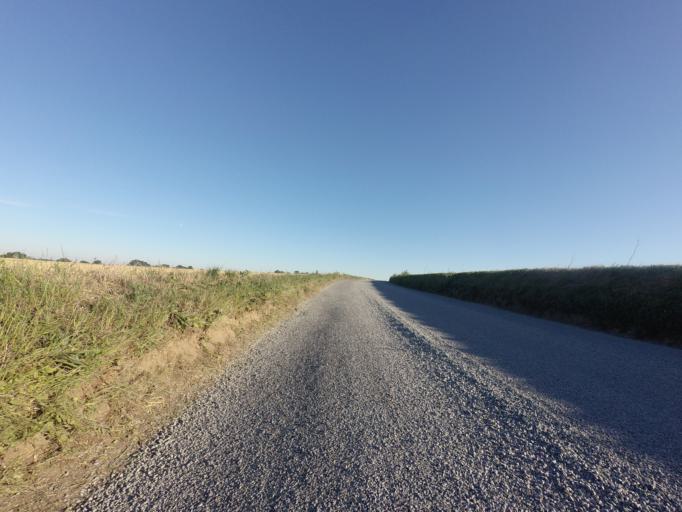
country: GB
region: England
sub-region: Kent
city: Herne Bay
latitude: 51.3408
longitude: 1.1898
